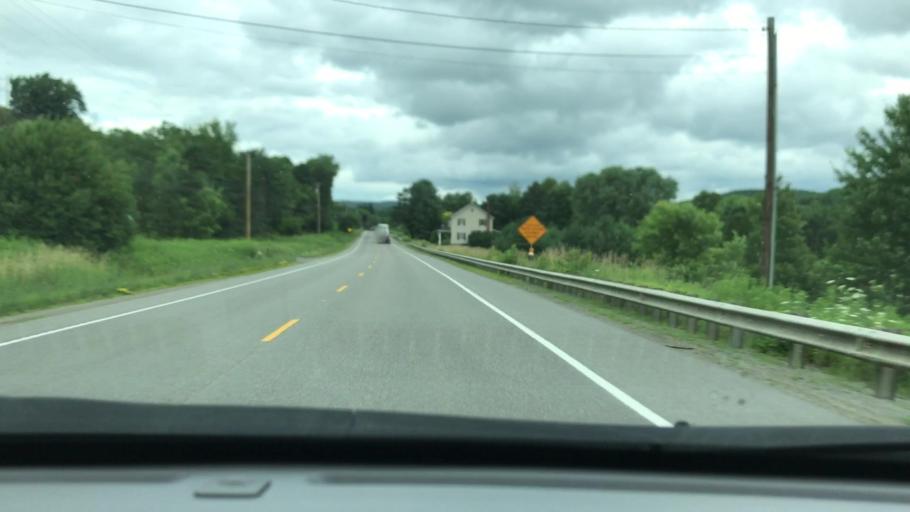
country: US
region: Pennsylvania
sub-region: Elk County
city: Ridgway
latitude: 41.3058
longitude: -78.6873
